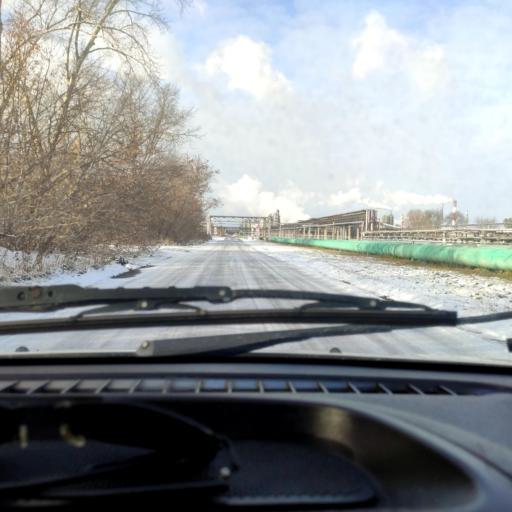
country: RU
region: Samara
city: Tol'yatti
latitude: 53.5350
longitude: 49.4765
